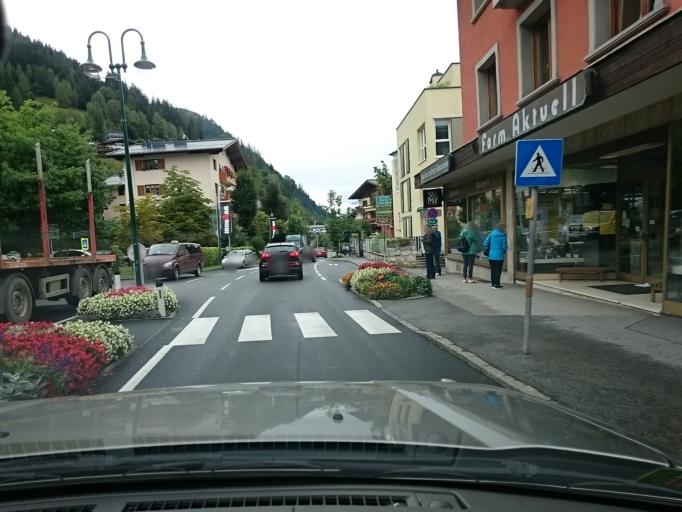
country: AT
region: Salzburg
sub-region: Politischer Bezirk Zell am See
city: Zell am See
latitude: 47.3261
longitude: 12.7966
